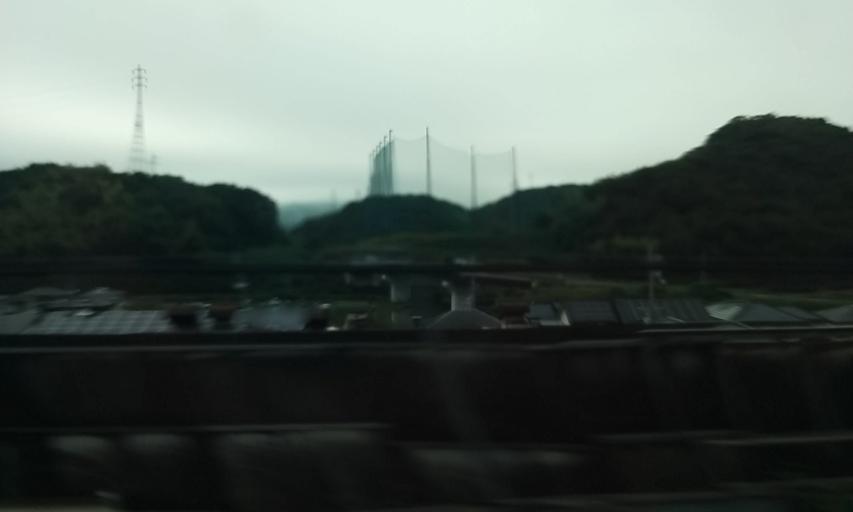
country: JP
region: Hyogo
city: Aioi
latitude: 34.8182
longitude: 134.5000
